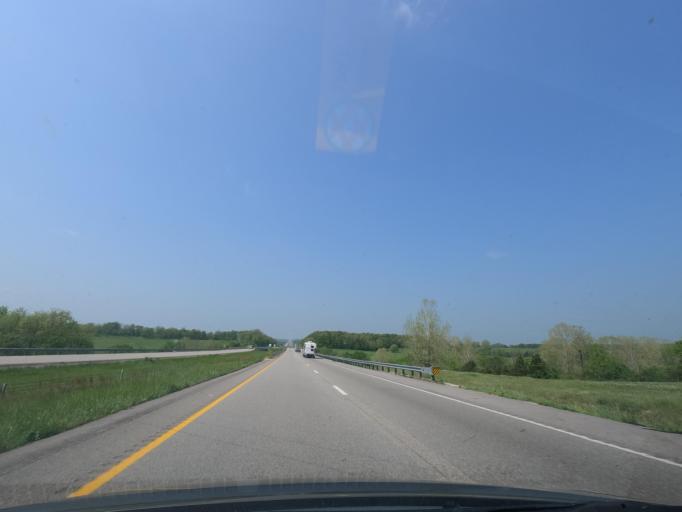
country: US
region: Missouri
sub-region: Christian County
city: Billings
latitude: 37.1782
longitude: -93.6578
